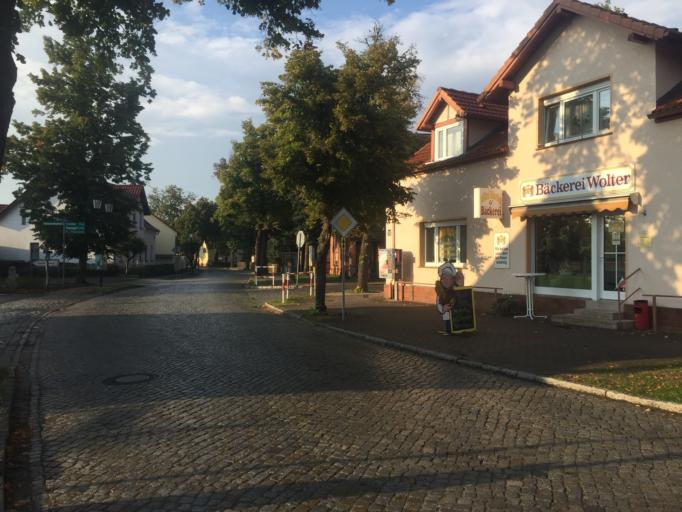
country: DE
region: Brandenburg
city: Mittenwalde
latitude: 52.2117
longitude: 13.5592
